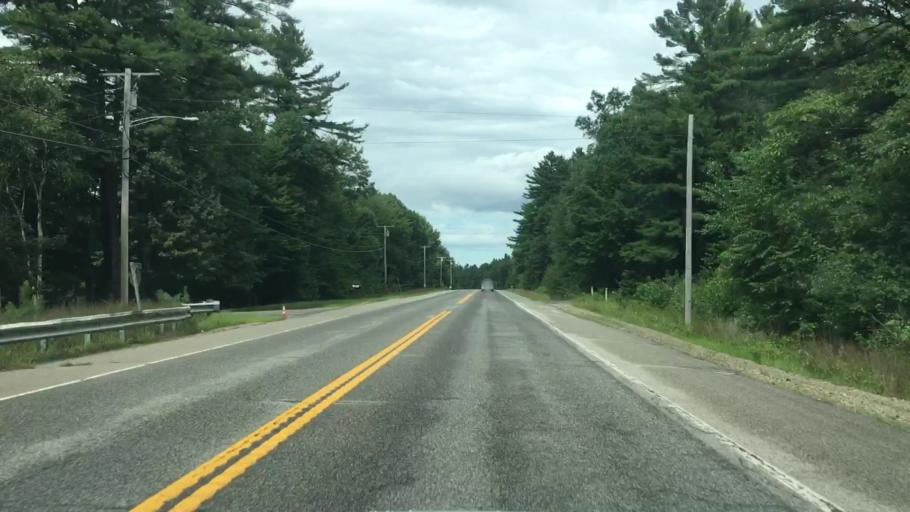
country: US
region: Maine
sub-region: York County
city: South Sanford
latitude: 43.3673
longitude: -70.7323
